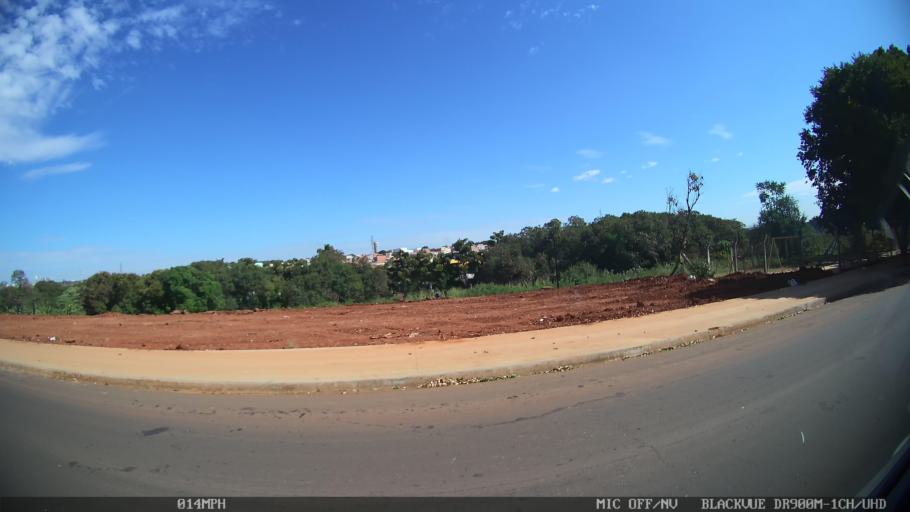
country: BR
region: Sao Paulo
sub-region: Santa Barbara D'Oeste
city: Santa Barbara d'Oeste
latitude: -22.7377
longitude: -47.3901
